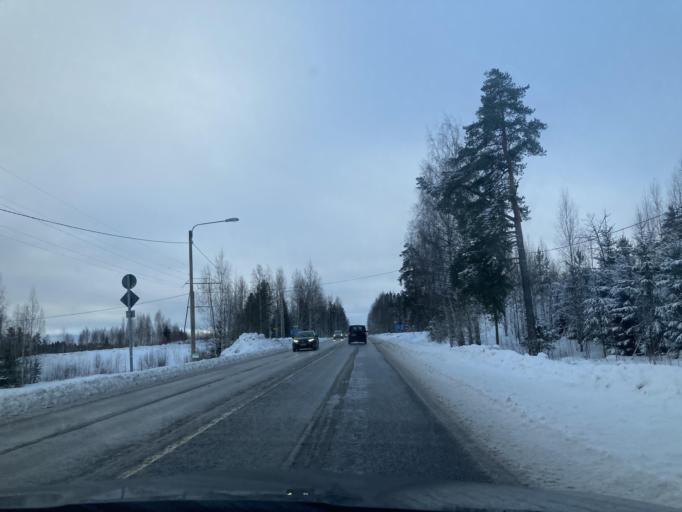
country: FI
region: Paijanne Tavastia
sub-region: Lahti
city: Lahti
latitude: 61.1091
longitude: 25.6418
